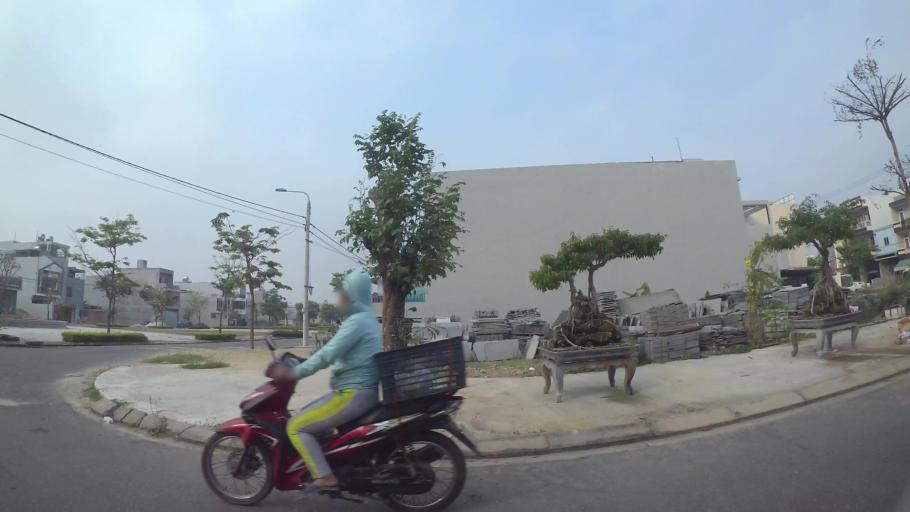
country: VN
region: Da Nang
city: Cam Le
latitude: 16.0141
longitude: 108.2221
